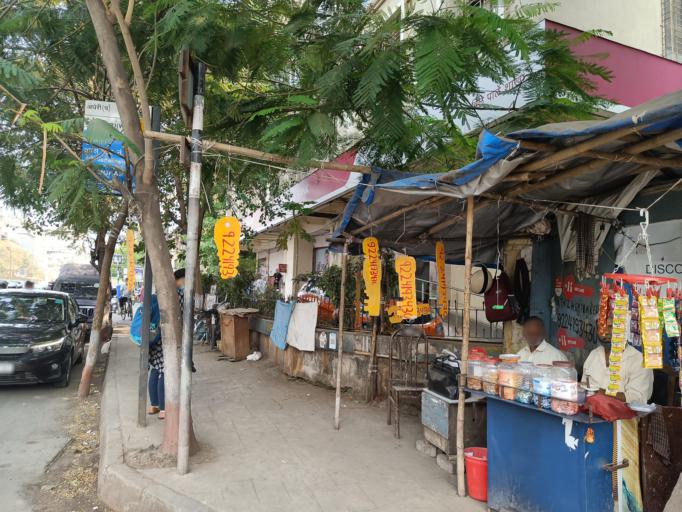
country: IN
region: Maharashtra
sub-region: Mumbai Suburban
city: Mumbai
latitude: 19.1159
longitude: 72.8307
